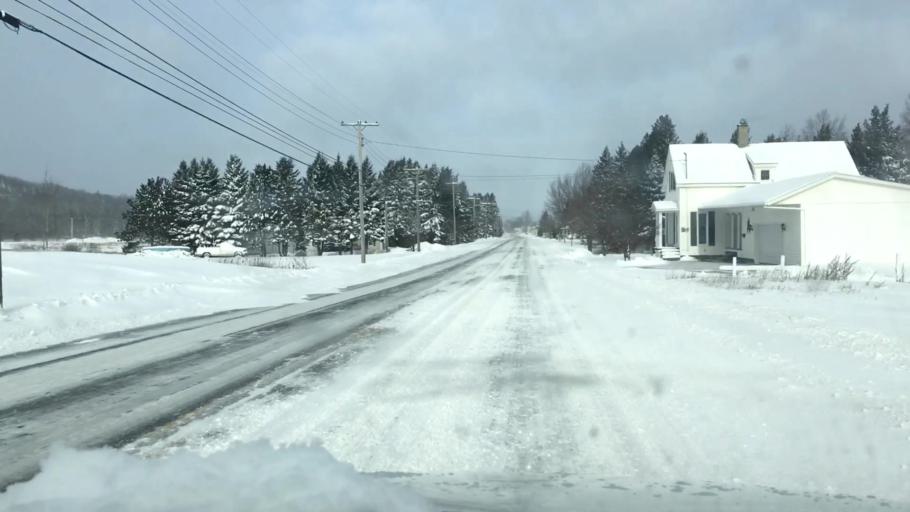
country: US
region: Maine
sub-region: Aroostook County
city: Van Buren
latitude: 47.1774
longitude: -67.9491
